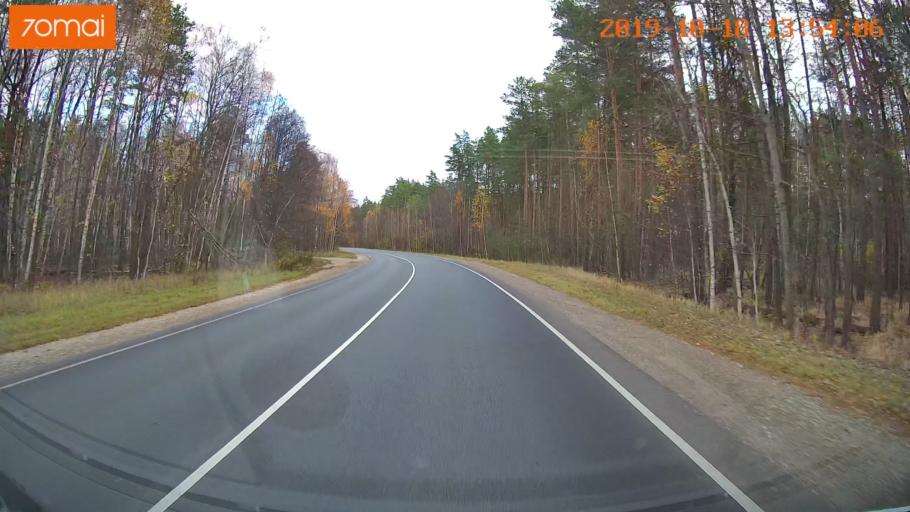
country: RU
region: Rjazan
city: Spas-Klepiki
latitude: 55.0394
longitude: 40.0005
